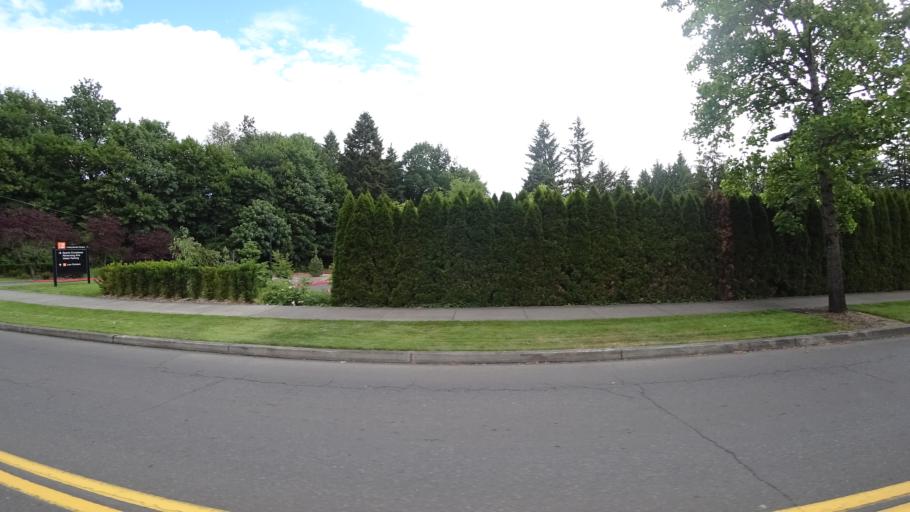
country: US
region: Oregon
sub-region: Clackamas County
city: Lake Oswego
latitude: 45.4523
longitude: -122.6740
